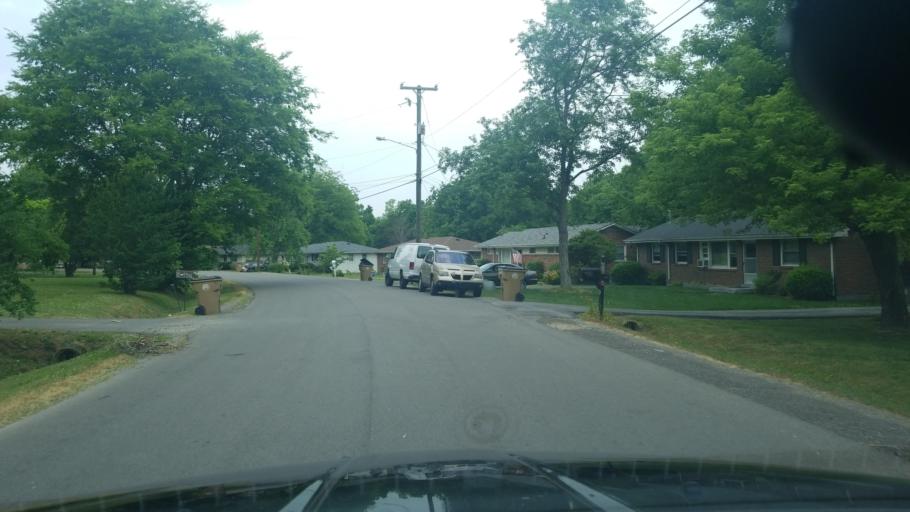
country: US
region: Tennessee
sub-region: Davidson County
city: Goodlettsville
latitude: 36.2642
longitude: -86.7479
